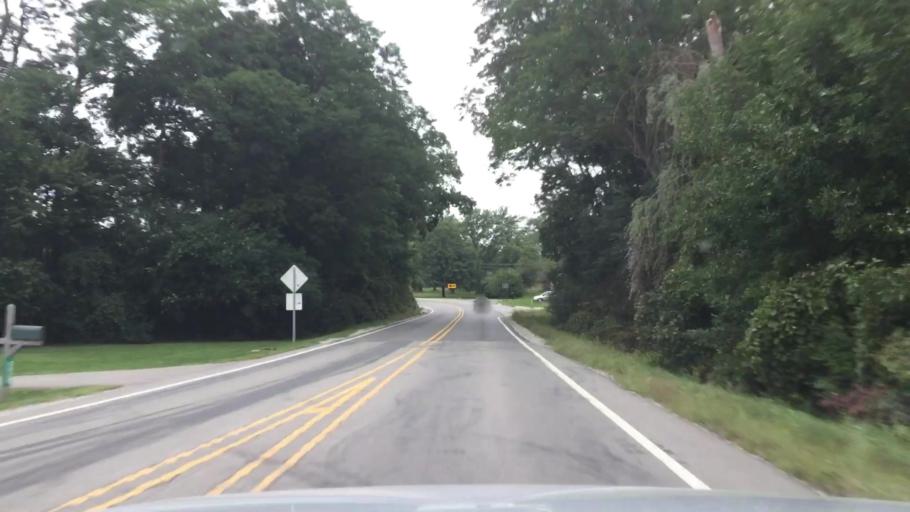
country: US
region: Michigan
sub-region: Washtenaw County
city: Ypsilanti
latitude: 42.2025
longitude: -83.6222
